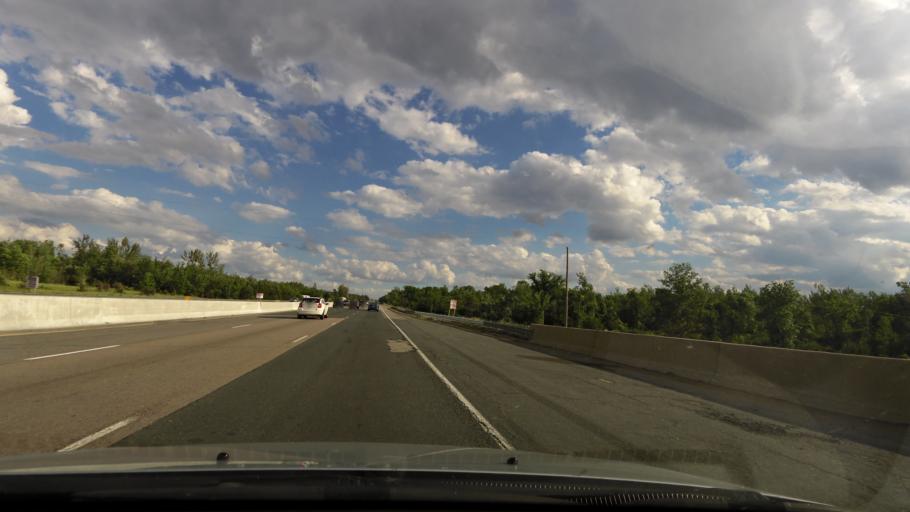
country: CA
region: Ontario
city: Bradford West Gwillimbury
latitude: 44.1741
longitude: -79.6443
